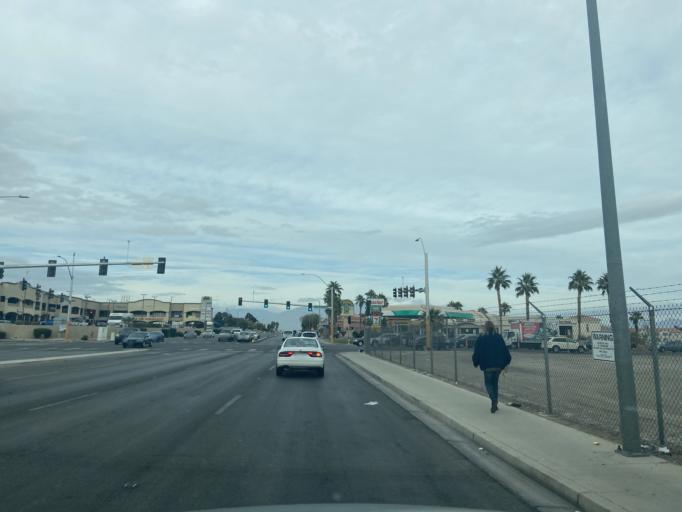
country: US
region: Nevada
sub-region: Clark County
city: Las Vegas
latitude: 36.2167
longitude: -115.2074
